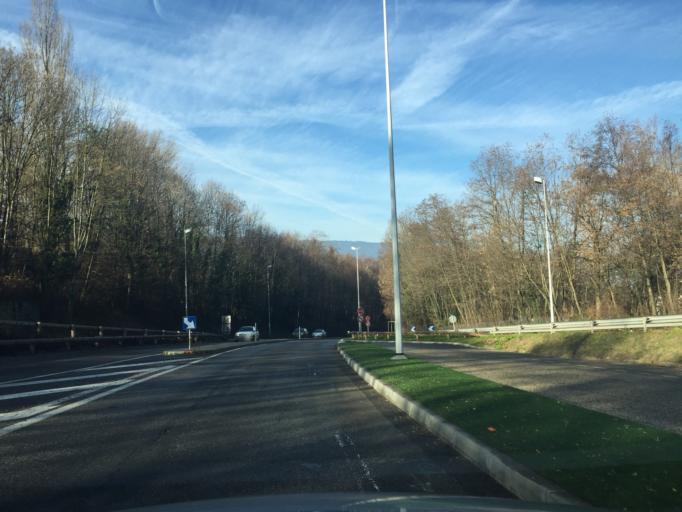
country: FR
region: Rhone-Alpes
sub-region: Departement de la Savoie
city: Bassens
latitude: 45.5918
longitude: 5.9152
